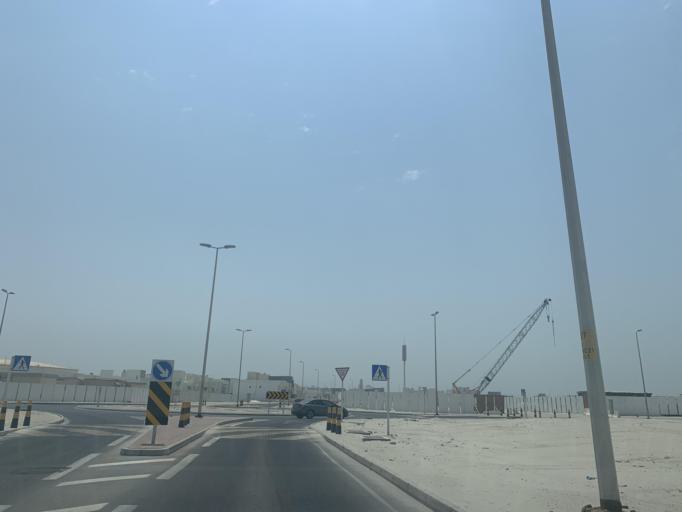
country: BH
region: Muharraq
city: Al Hadd
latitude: 26.2338
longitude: 50.6665
